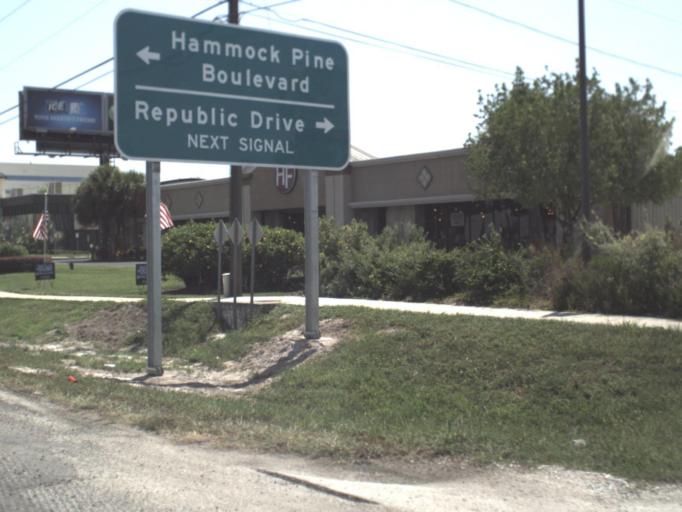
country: US
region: Florida
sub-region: Pinellas County
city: Saint George
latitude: 28.0304
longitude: -82.7384
